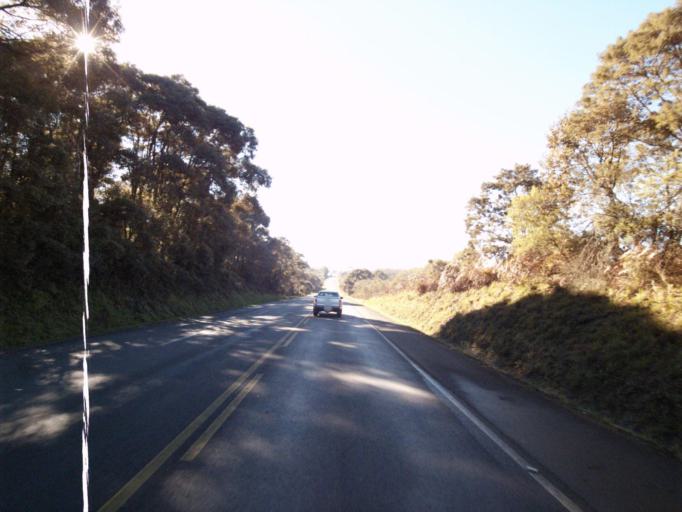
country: BR
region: Santa Catarina
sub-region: Concordia
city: Concordia
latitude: -26.9200
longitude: -51.9366
